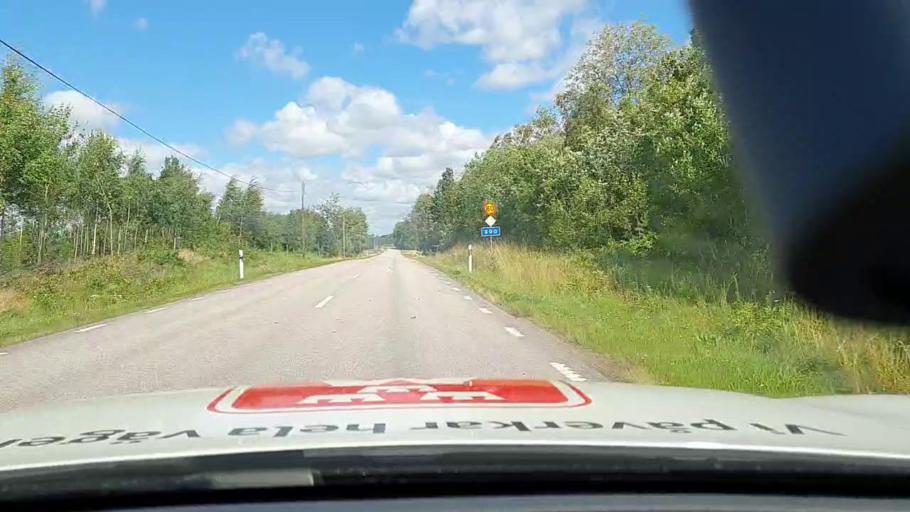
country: SE
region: Vaestra Goetaland
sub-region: Skovde Kommun
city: Stopen
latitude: 58.5245
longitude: 13.9852
